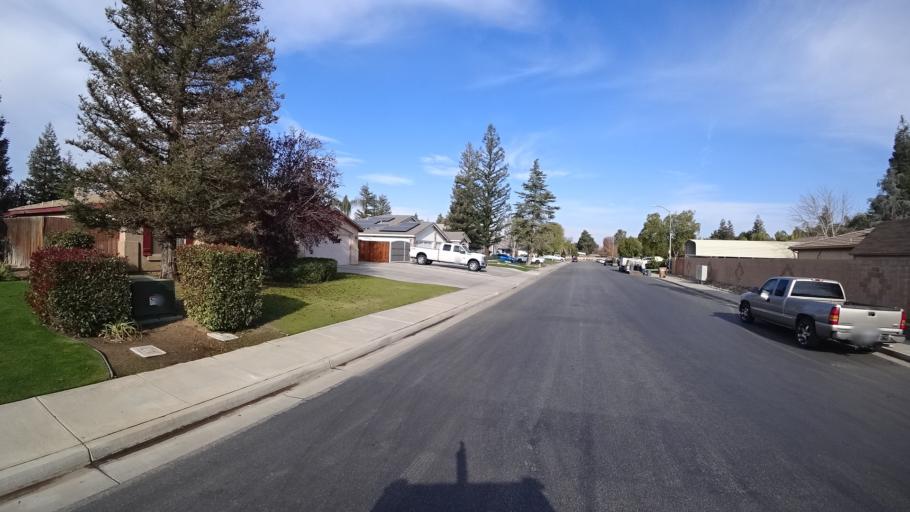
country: US
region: California
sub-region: Kern County
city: Greenacres
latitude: 35.4082
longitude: -119.0695
